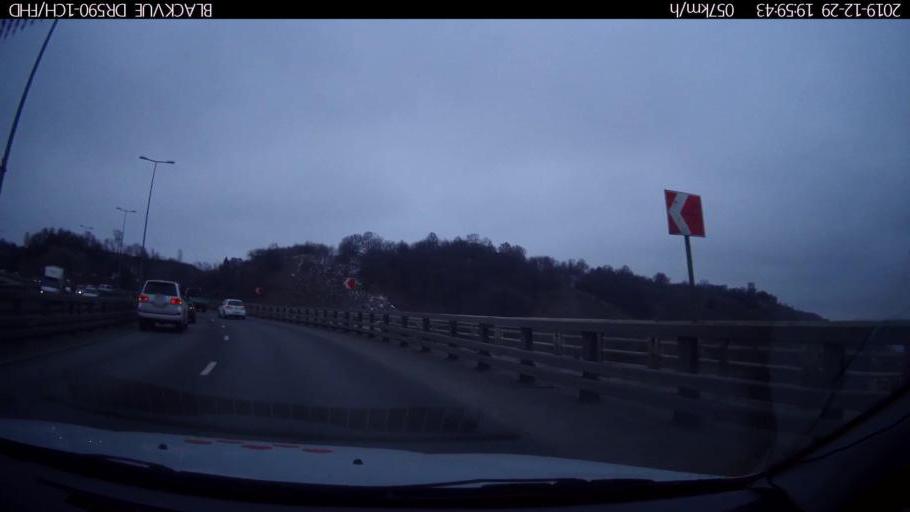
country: RU
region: Nizjnij Novgorod
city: Nizhniy Novgorod
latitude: 56.3174
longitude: 43.9692
